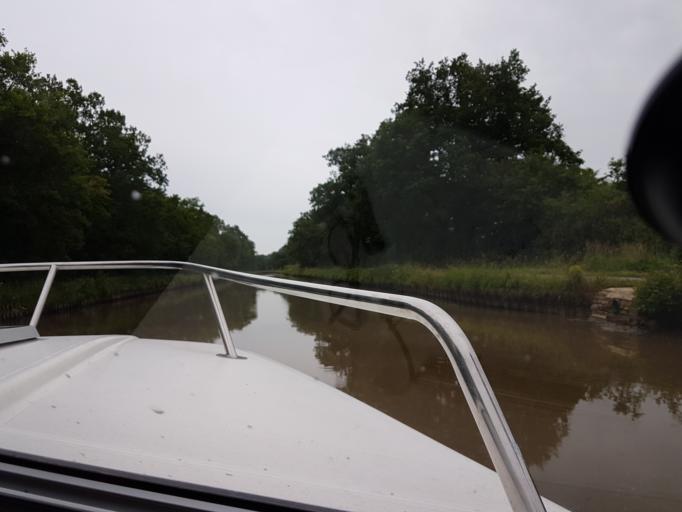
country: FR
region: Bourgogne
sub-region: Departement de la Nievre
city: Clamecy
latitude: 47.3771
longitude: 3.6044
